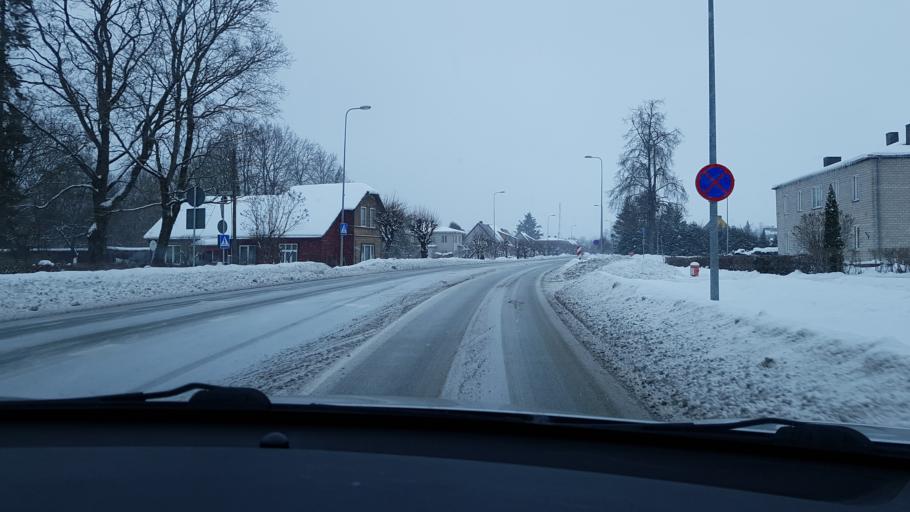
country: EE
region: Jaervamaa
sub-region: Tueri vald
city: Tueri
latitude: 58.8114
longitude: 25.4287
